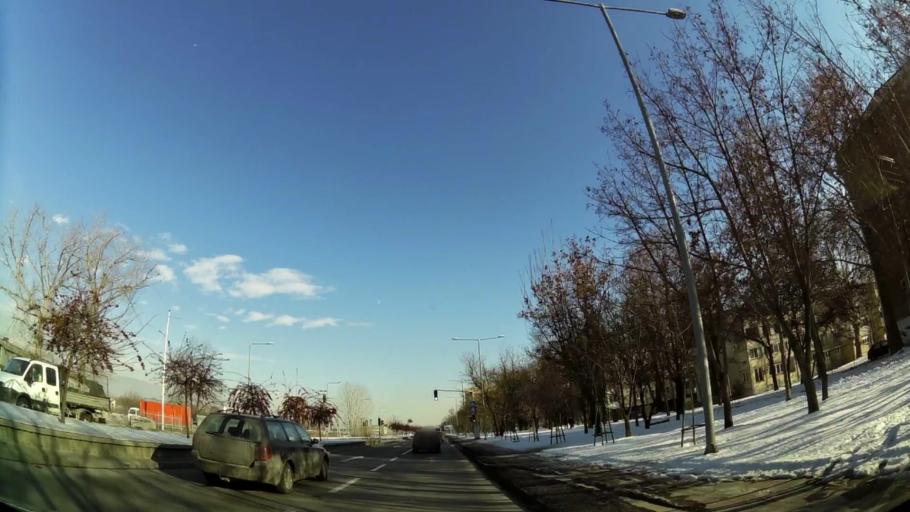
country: MK
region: Karpos
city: Skopje
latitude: 42.0075
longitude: 21.3960
